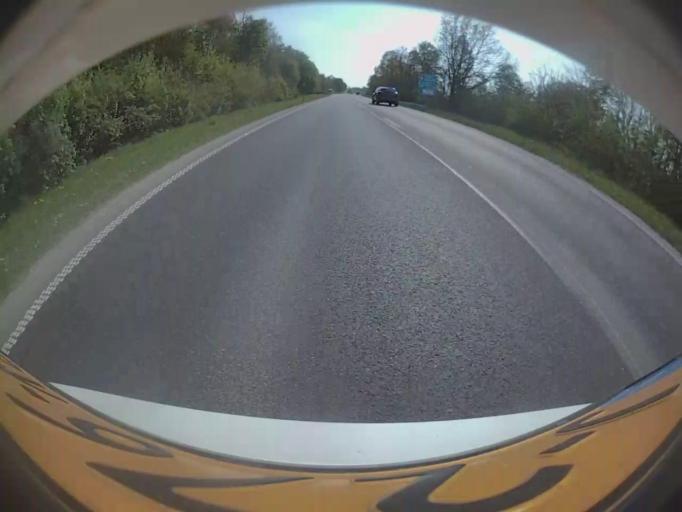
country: BE
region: Wallonia
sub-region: Province de Namur
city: Ciney
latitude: 50.2959
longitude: 5.1168
